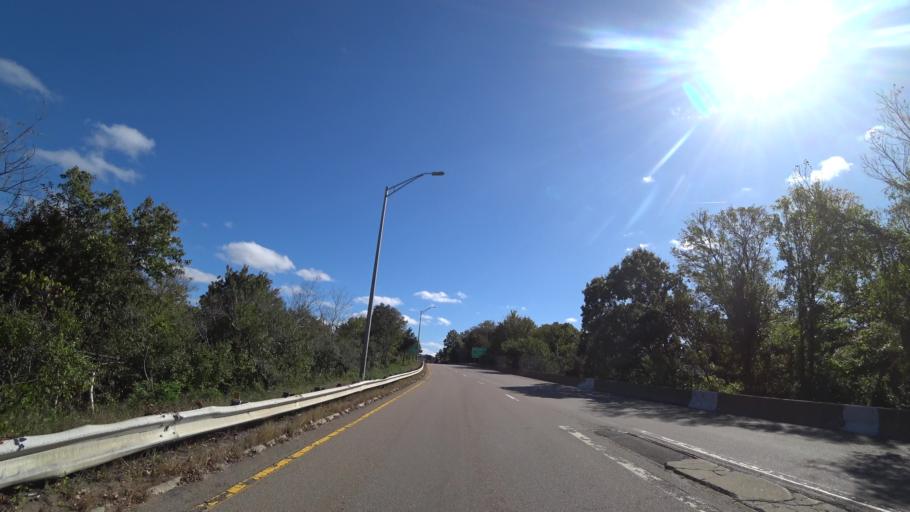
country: US
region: Massachusetts
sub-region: Norfolk County
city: Braintree
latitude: 42.2264
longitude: -71.0068
